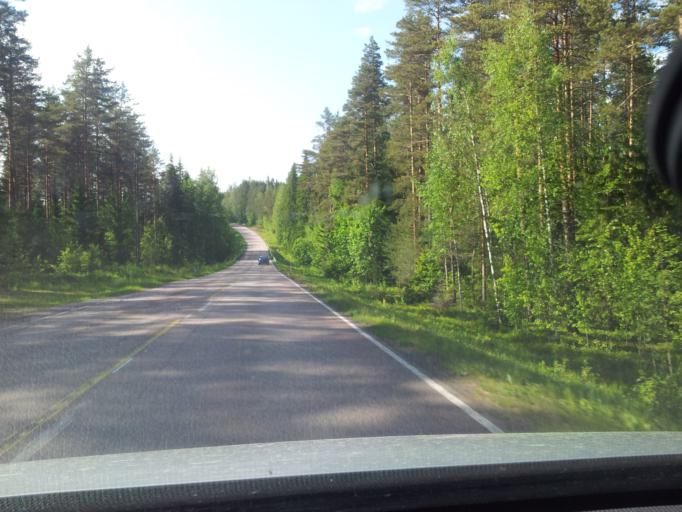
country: FI
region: South Karelia
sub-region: Lappeenranta
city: Luumaeki
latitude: 60.9613
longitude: 27.5744
